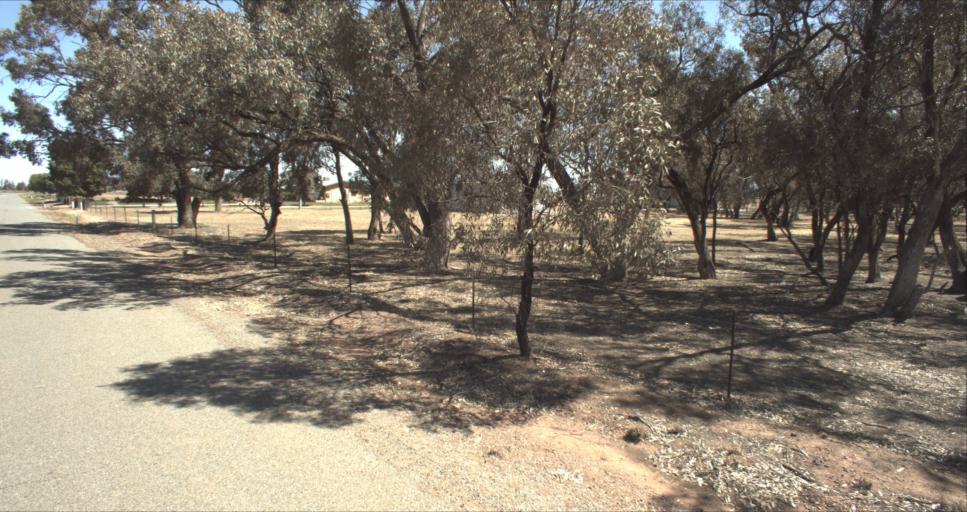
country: AU
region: New South Wales
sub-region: Leeton
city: Leeton
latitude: -34.5001
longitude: 146.4205
